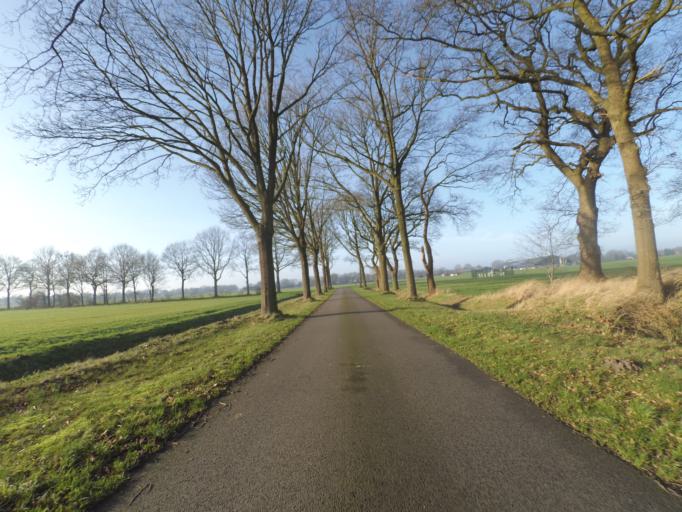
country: NL
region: Drenthe
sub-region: Gemeente Borger-Odoorn
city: Borger
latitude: 52.8801
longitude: 6.6553
